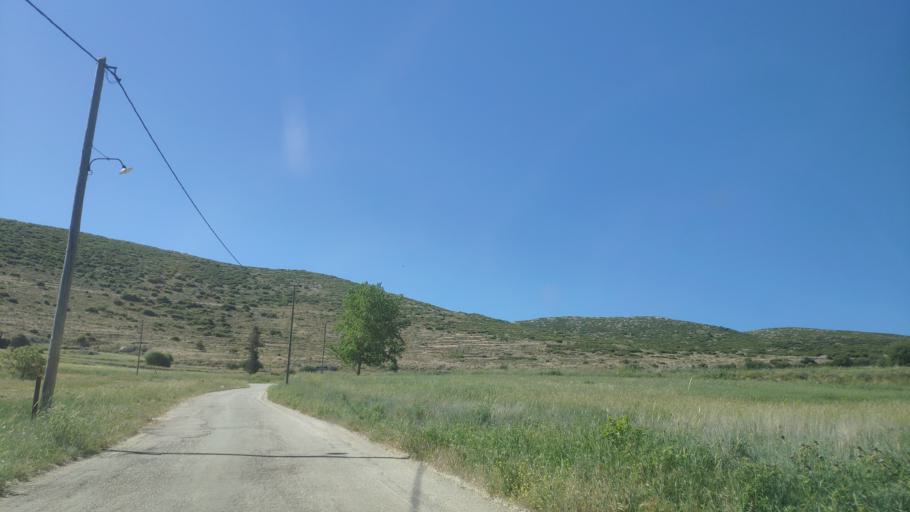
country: GR
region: Peloponnese
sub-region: Nomos Korinthias
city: Khiliomodhi
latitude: 37.7525
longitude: 22.8741
